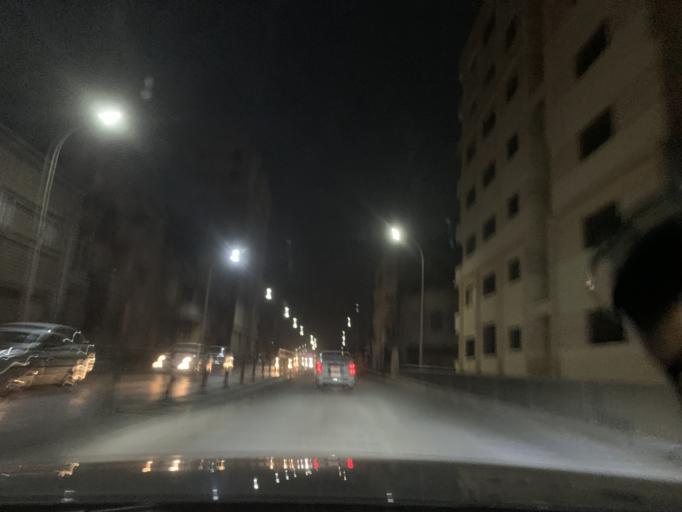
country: EG
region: Muhafazat al Qahirah
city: Cairo
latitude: 30.0854
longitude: 31.2943
